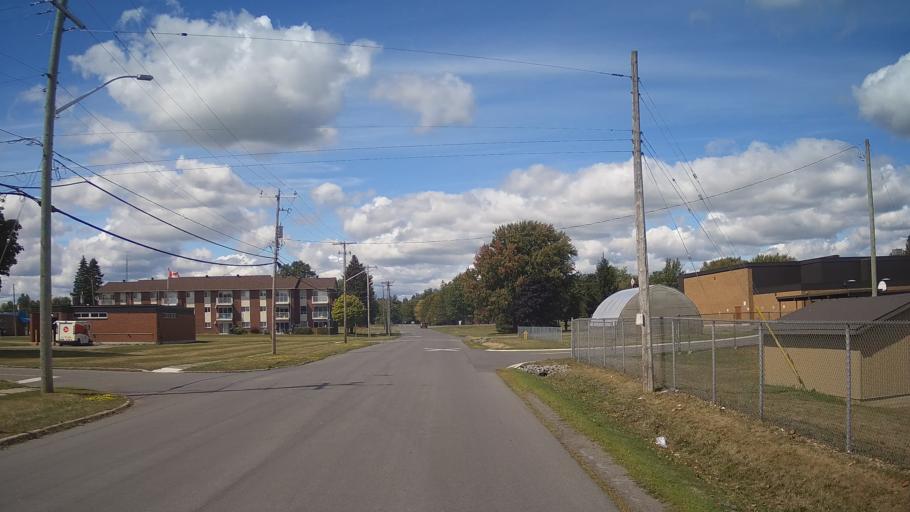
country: US
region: New York
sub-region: St. Lawrence County
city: Ogdensburg
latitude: 44.8494
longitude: -75.3144
